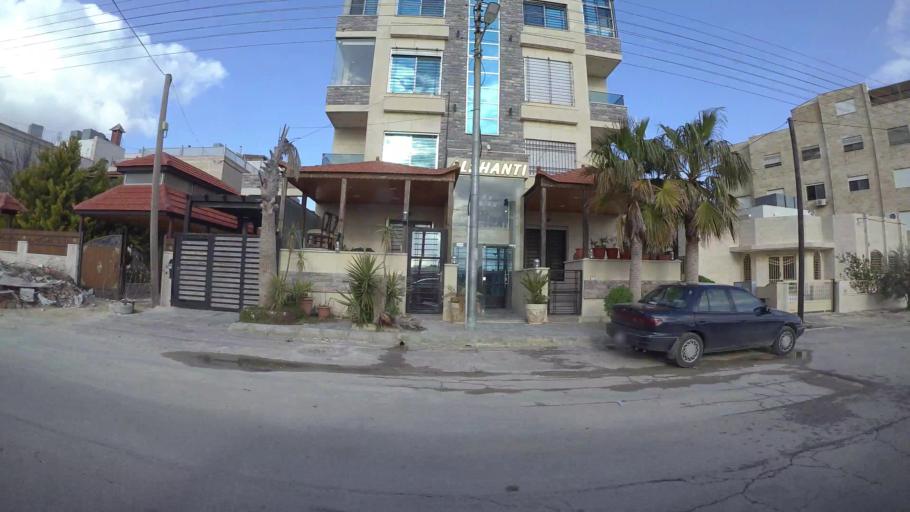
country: JO
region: Amman
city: Al Bunayyat ash Shamaliyah
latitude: 31.9086
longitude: 35.8804
